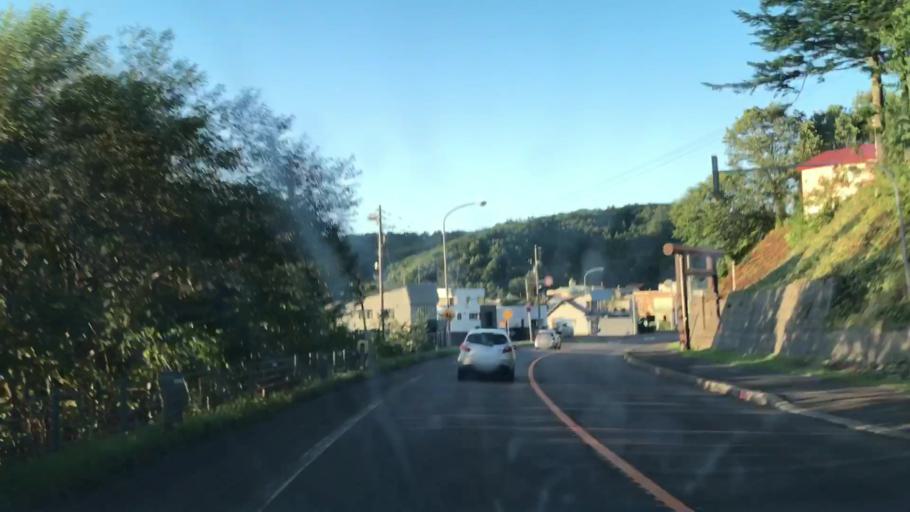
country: JP
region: Hokkaido
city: Niseko Town
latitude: 42.7924
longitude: 140.9349
